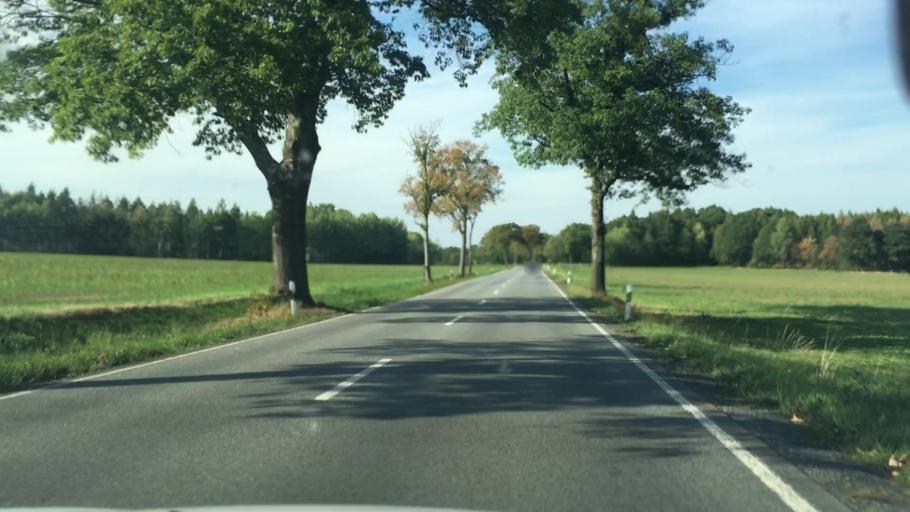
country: DE
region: Saxony
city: Dohma
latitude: 50.8860
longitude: 13.9535
